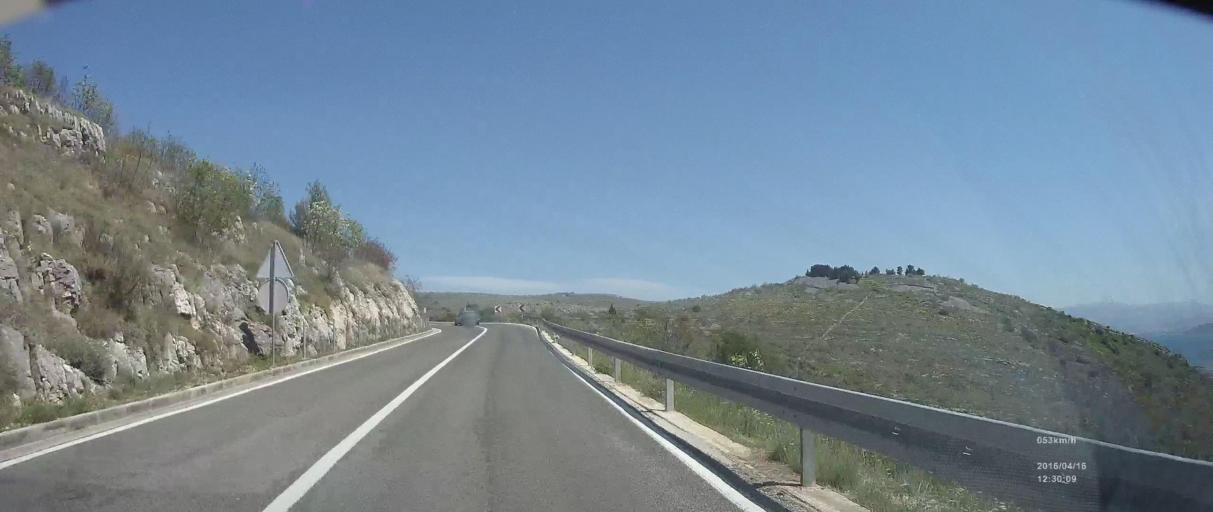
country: HR
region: Splitsko-Dalmatinska
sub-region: Grad Trogir
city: Trogir
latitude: 43.5281
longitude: 16.2174
